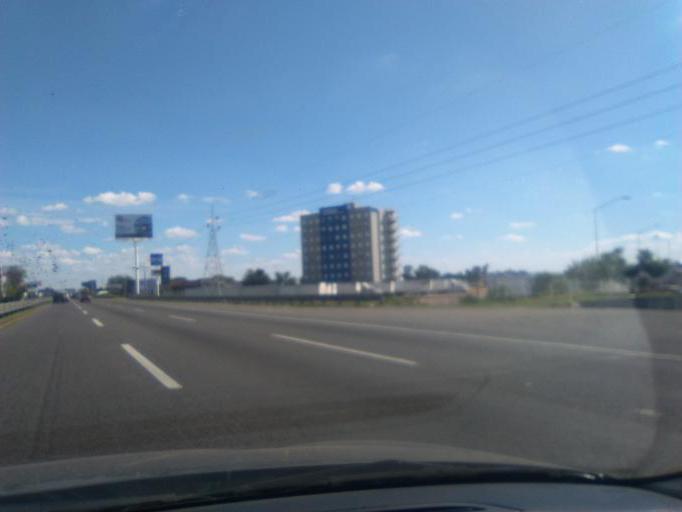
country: MX
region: Guanajuato
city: Colonia Nuevo Mexico
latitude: 20.9666
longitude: -101.4577
